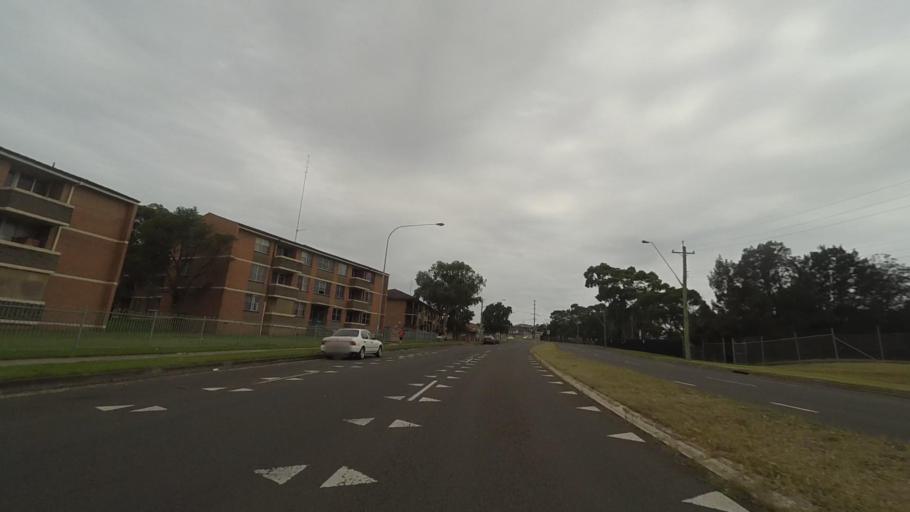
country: AU
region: New South Wales
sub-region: Wollongong
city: Port Kembla
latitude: -34.4880
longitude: 150.8923
